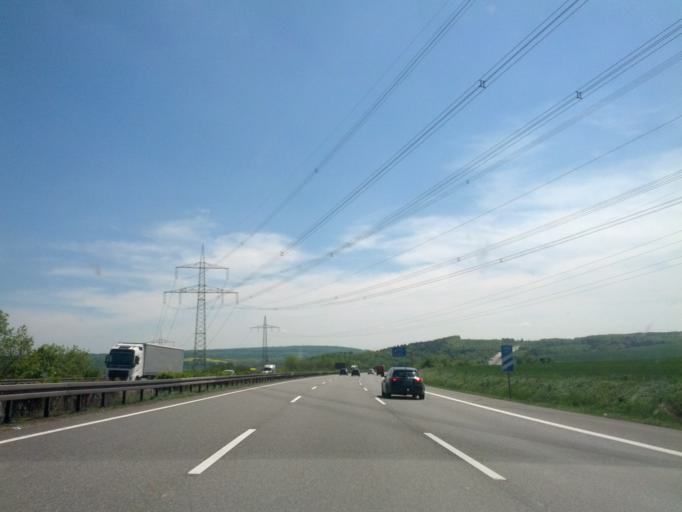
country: DE
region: Thuringia
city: Mellingen
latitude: 50.9354
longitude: 11.3817
